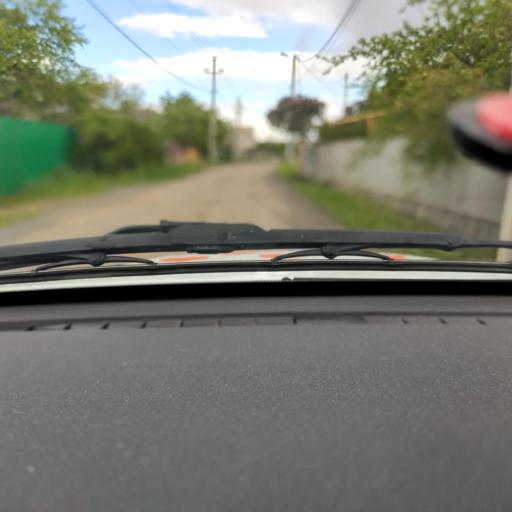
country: RU
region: Voronezj
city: Podgornoye
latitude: 51.7427
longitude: 39.1527
